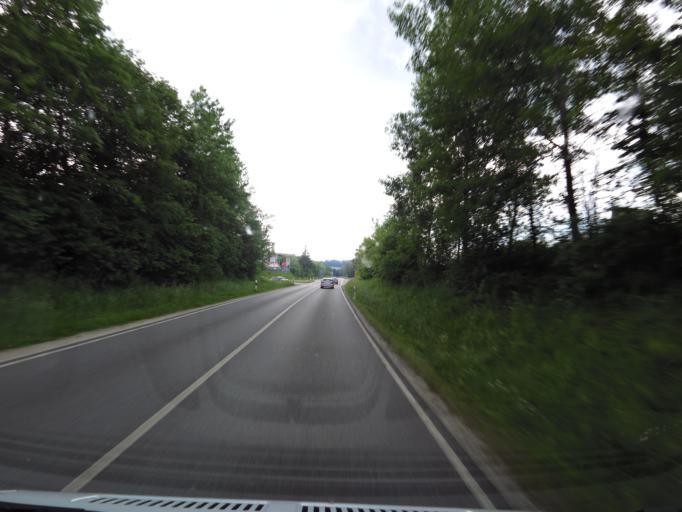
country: DE
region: Bavaria
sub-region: Lower Bavaria
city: Aicha vorm Wald
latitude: 48.6797
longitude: 13.2982
